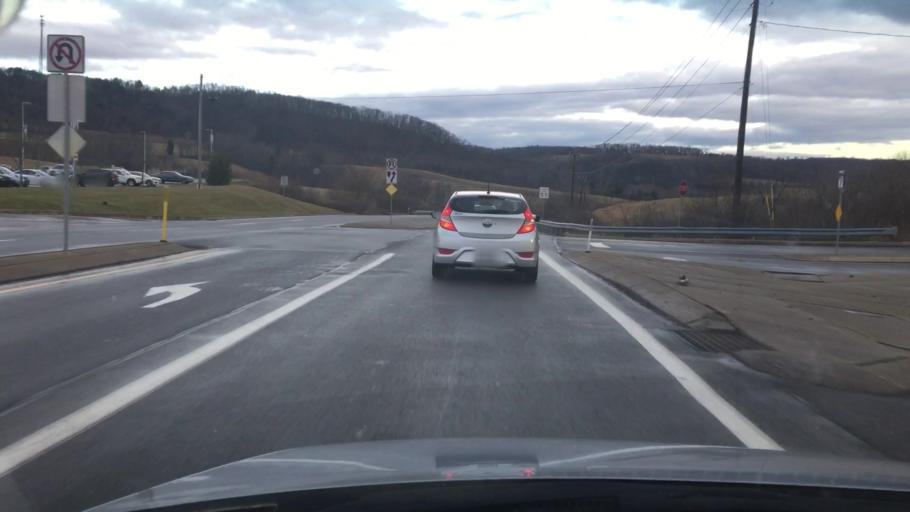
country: US
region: Pennsylvania
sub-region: Columbia County
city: Bloomsburg
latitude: 41.0191
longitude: -76.4897
